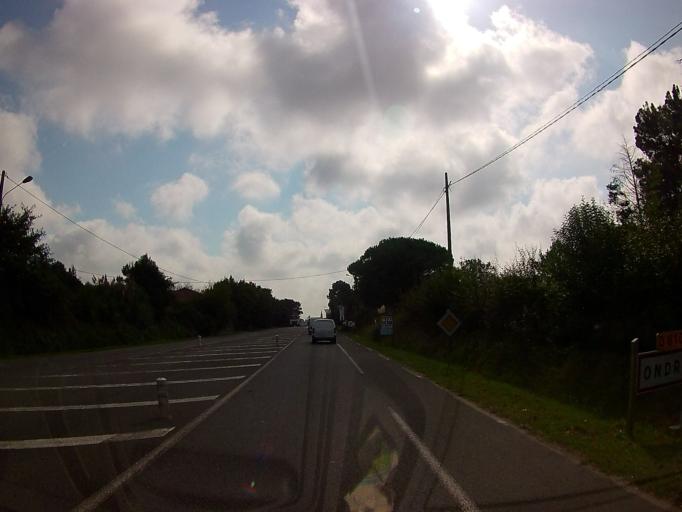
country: FR
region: Aquitaine
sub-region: Departement des Landes
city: Ondres
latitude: 43.5700
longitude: -1.4415
